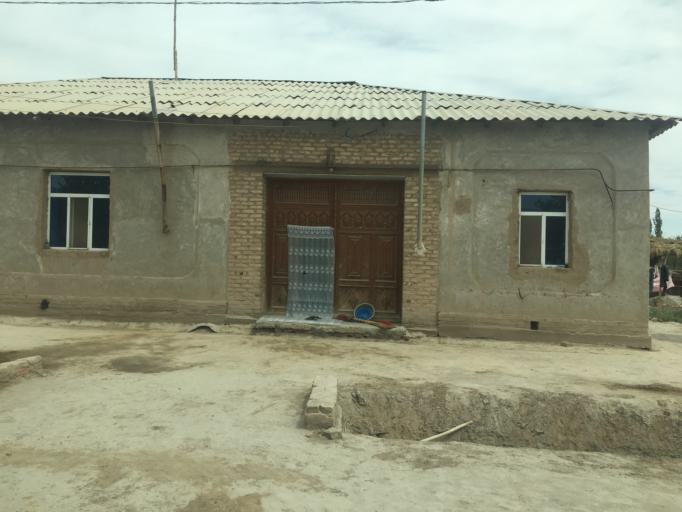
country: TM
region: Dasoguz
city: Tagta
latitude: 41.6137
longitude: 59.8542
